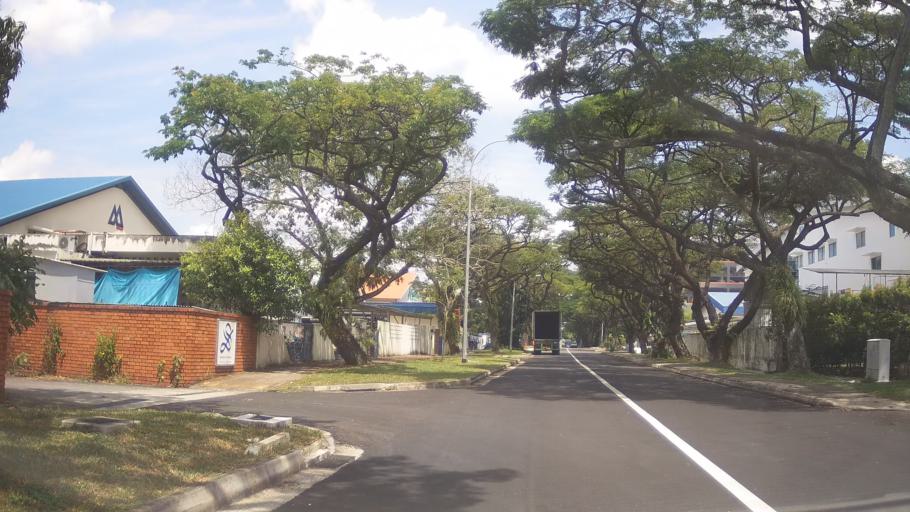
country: SG
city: Singapore
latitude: 1.3307
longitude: 103.7147
